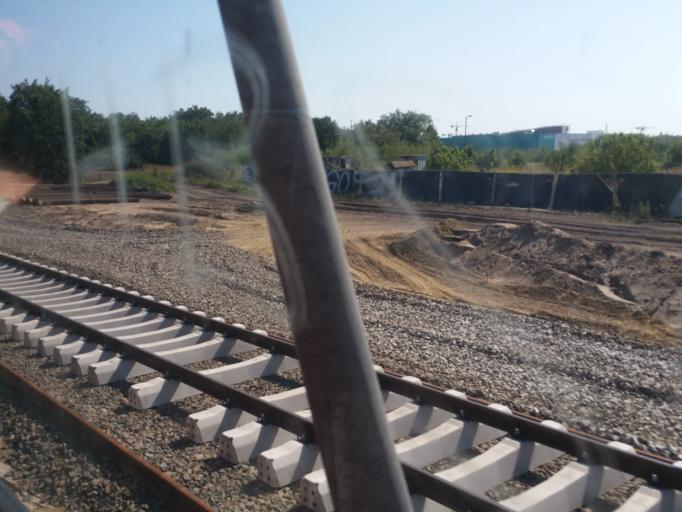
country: DE
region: Berlin
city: Adlershof
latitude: 52.4423
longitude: 13.5306
